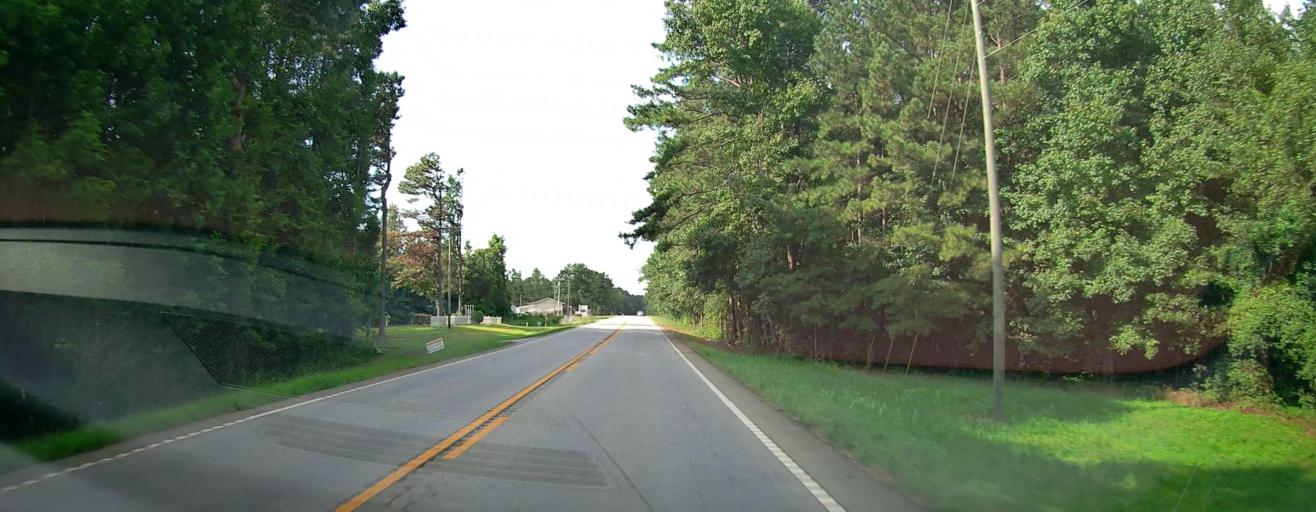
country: US
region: Georgia
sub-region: Coweta County
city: Senoia
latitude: 33.2354
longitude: -84.5665
